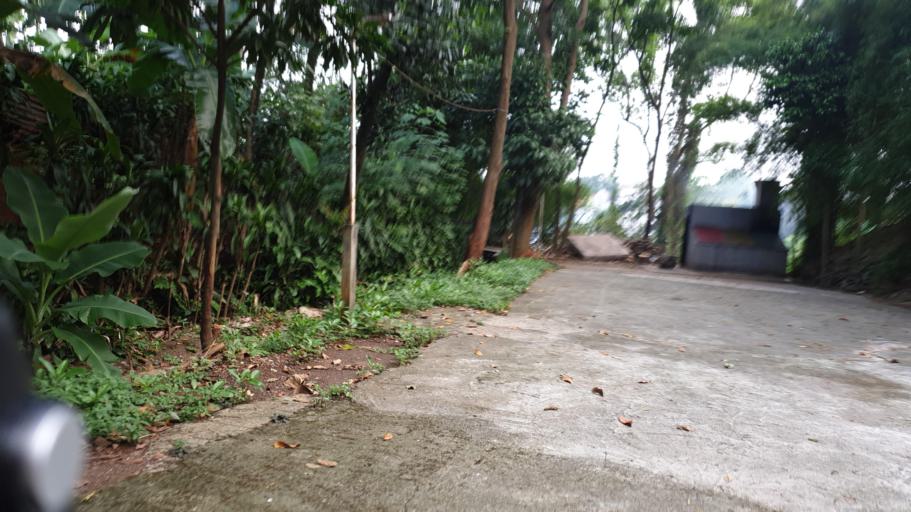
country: ID
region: West Java
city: Depok
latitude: -6.3701
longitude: 106.8386
